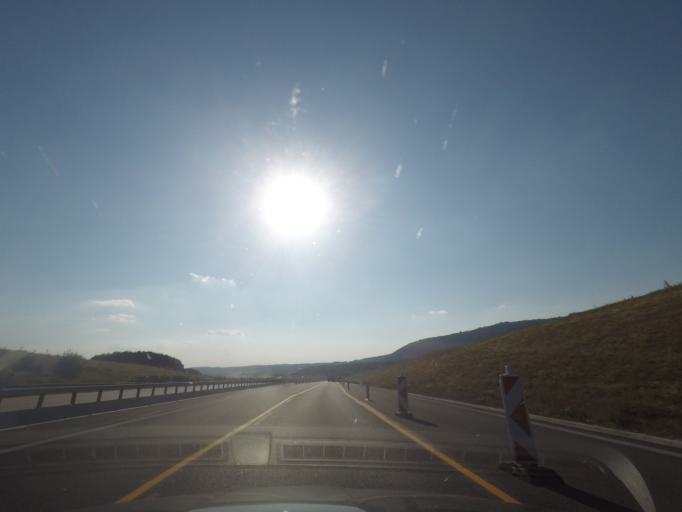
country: CZ
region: Olomoucky
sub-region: Okres Prerov
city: Lipnik nad Becvou
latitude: 49.5477
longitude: 17.5770
